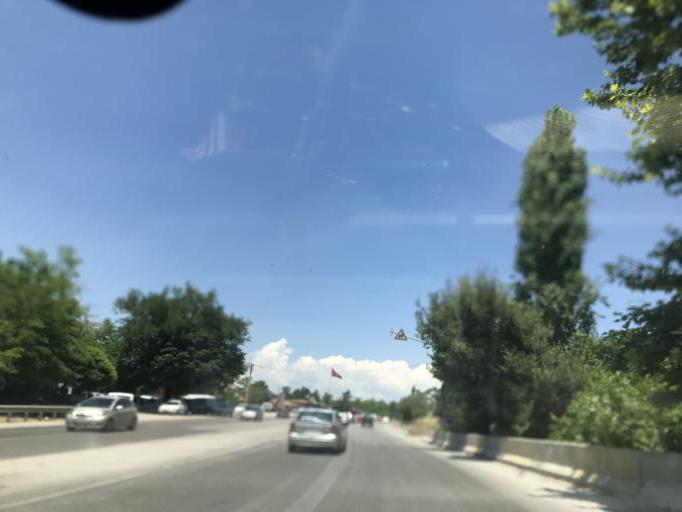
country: TR
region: Denizli
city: Denizli
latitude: 37.7283
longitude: 29.1678
